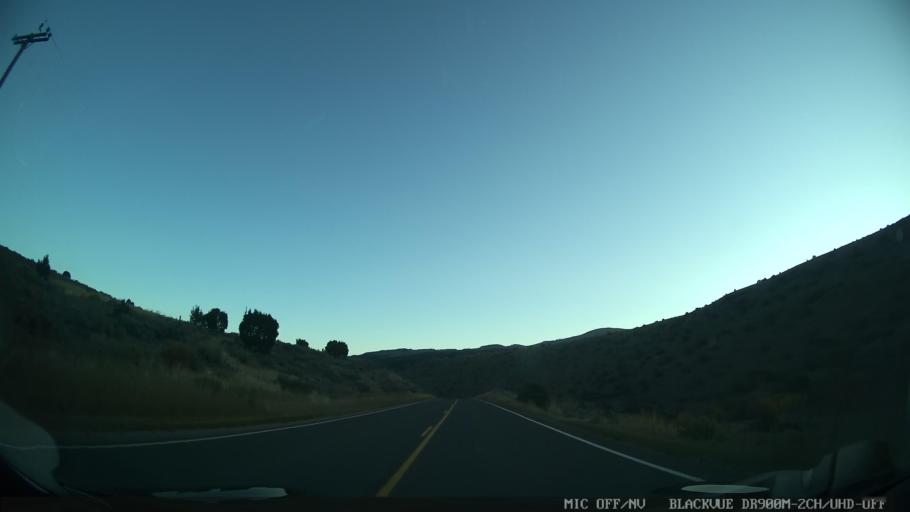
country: US
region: Colorado
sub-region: Eagle County
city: Edwards
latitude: 39.8287
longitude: -106.6398
